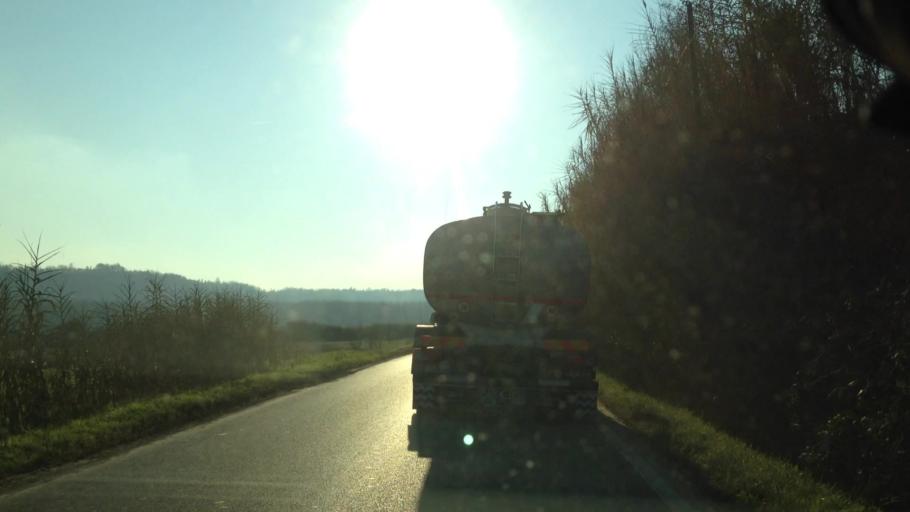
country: IT
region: Piedmont
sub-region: Provincia di Alessandria
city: Masio
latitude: 44.8500
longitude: 8.4003
